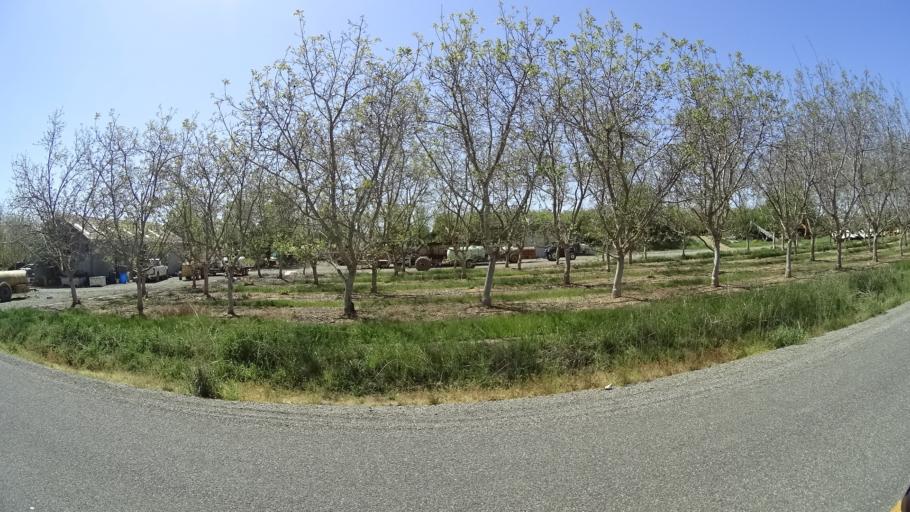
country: US
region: California
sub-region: Glenn County
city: Orland
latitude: 39.7867
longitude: -122.1444
